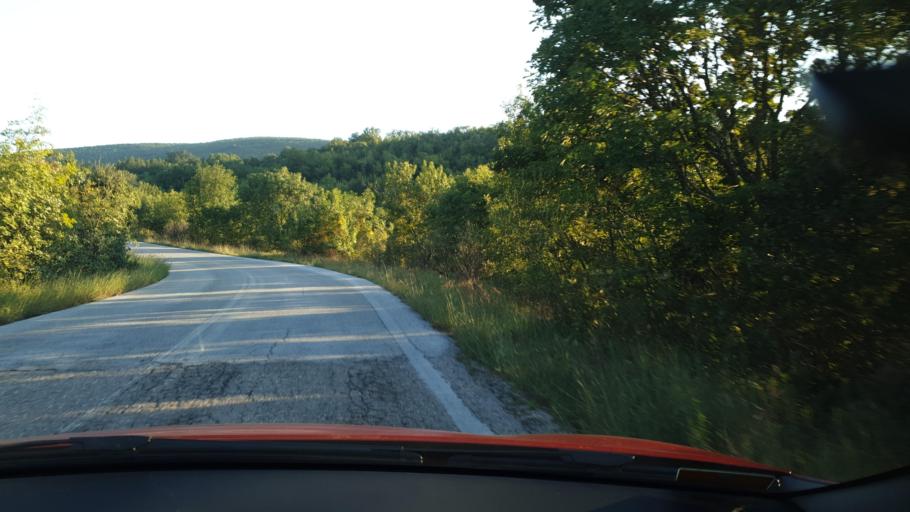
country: GR
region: Central Macedonia
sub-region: Nomos Chalkidikis
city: Galatista
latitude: 40.5515
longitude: 23.2837
